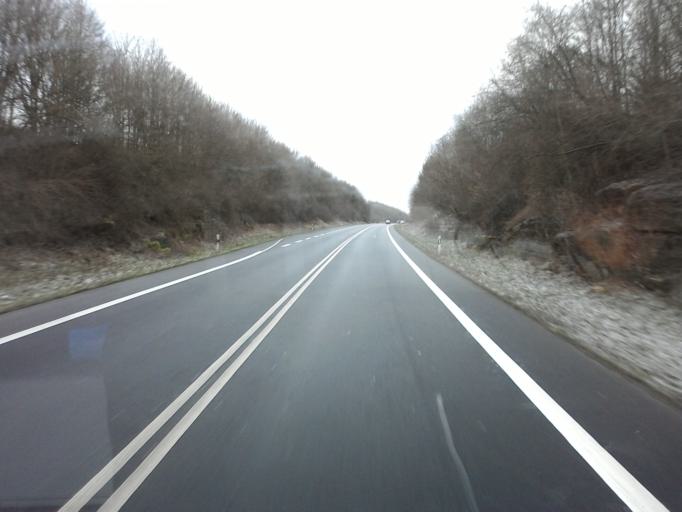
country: DE
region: Rheinland-Pfalz
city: Fliessem
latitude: 50.0183
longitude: 6.5335
